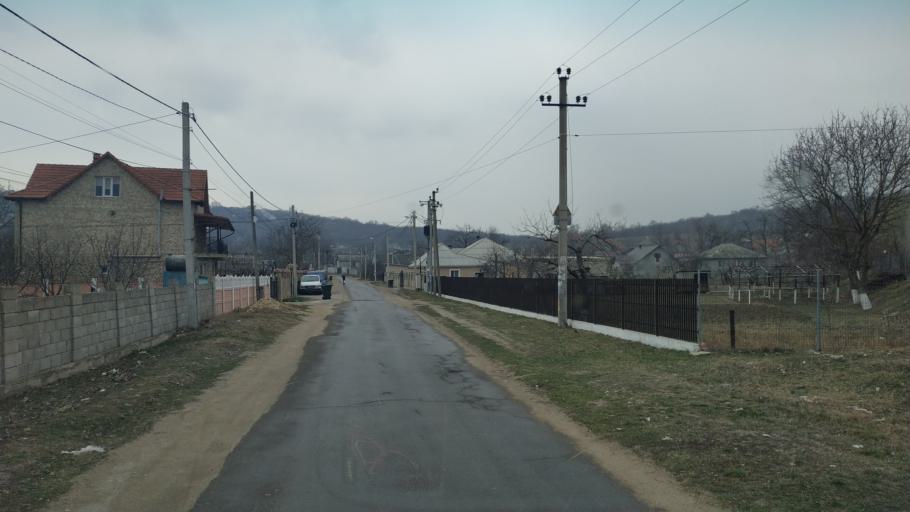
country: MD
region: Chisinau
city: Singera
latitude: 46.9138
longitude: 28.9756
